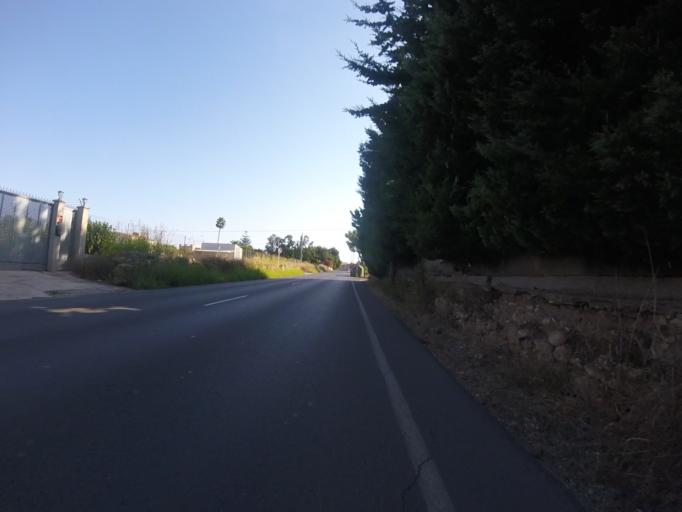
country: ES
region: Valencia
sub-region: Provincia de Castello
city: Benicarlo
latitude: 40.4098
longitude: 0.4198
